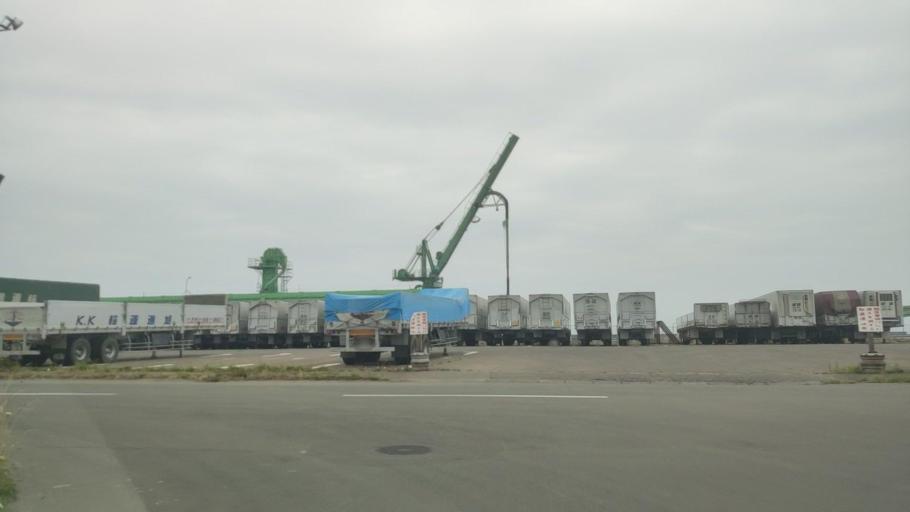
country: JP
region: Hokkaido
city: Otaru
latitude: 43.1876
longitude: 141.0236
